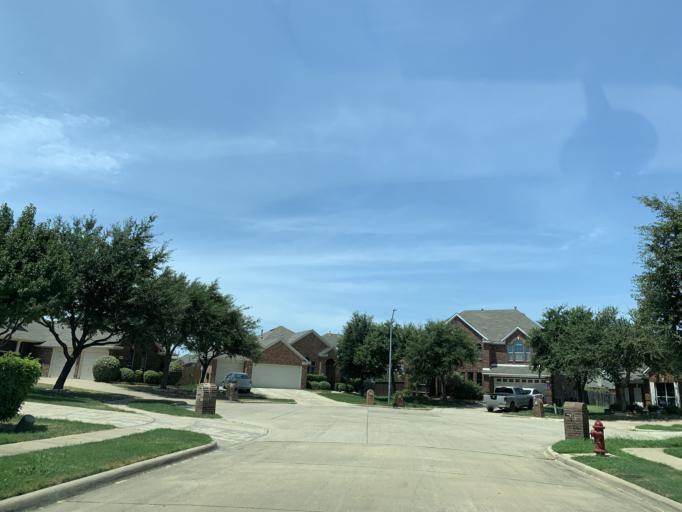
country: US
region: Texas
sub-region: Dallas County
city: Cedar Hill
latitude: 32.6487
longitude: -97.0393
